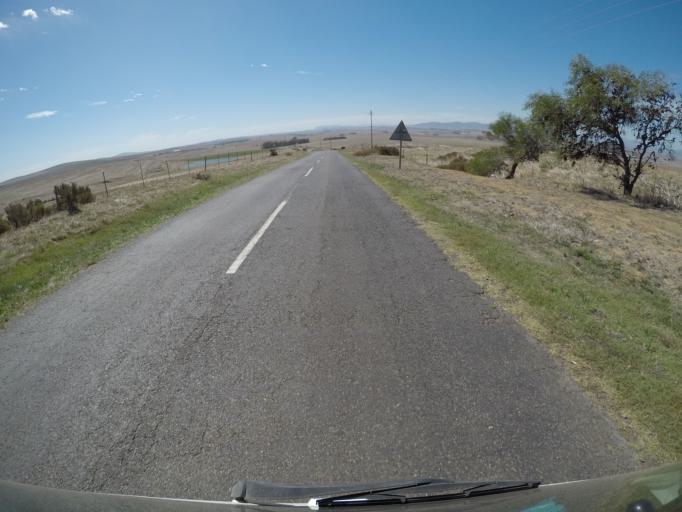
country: ZA
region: Western Cape
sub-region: City of Cape Town
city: Sunset Beach
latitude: -33.7084
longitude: 18.5842
